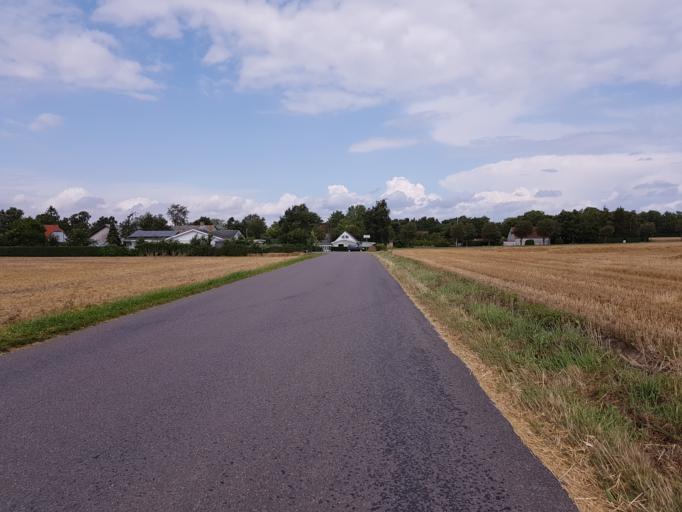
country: DK
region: Zealand
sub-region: Guldborgsund Kommune
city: Nykobing Falster
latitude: 54.5994
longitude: 11.9424
